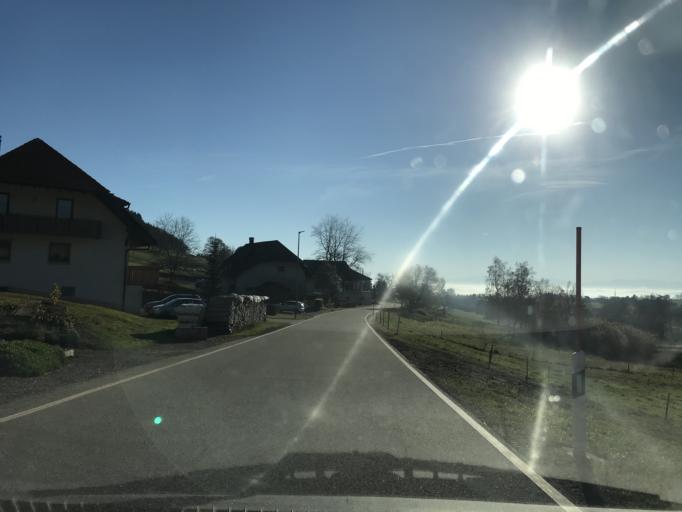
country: DE
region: Baden-Wuerttemberg
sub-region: Freiburg Region
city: Rickenbach
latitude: 47.6405
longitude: 7.9705
